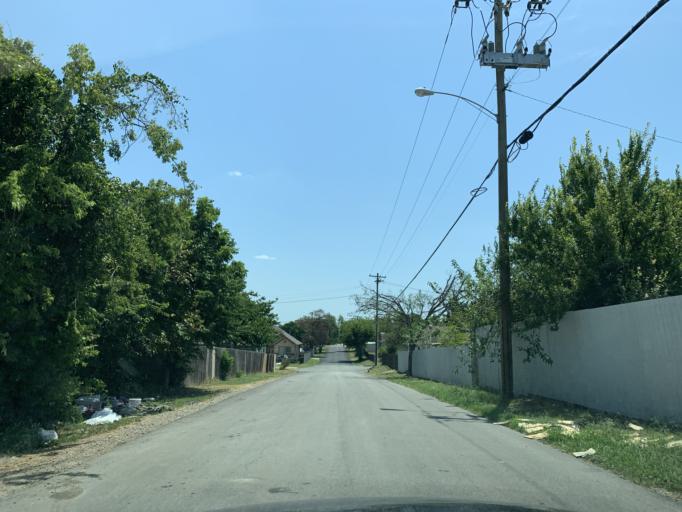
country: US
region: Texas
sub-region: Dallas County
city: Dallas
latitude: 32.6942
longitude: -96.7999
